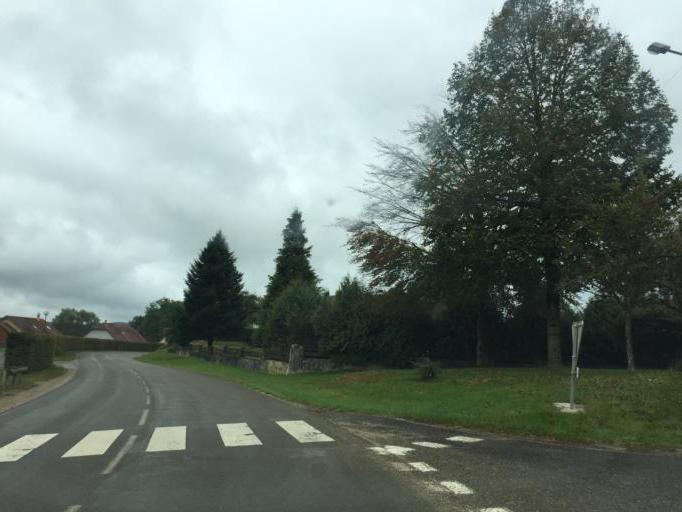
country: FR
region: Franche-Comte
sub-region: Departement du Jura
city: Orgelet
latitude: 46.5586
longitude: 5.6056
